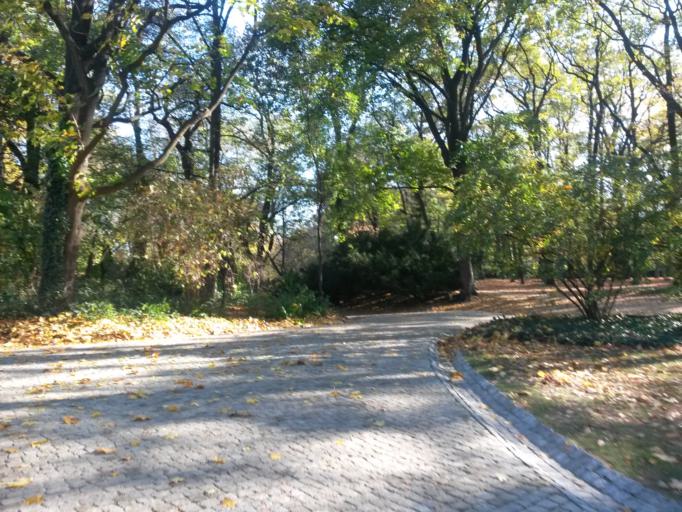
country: PL
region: Masovian Voivodeship
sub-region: Warszawa
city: Srodmiescie
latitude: 52.2163
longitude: 21.0267
